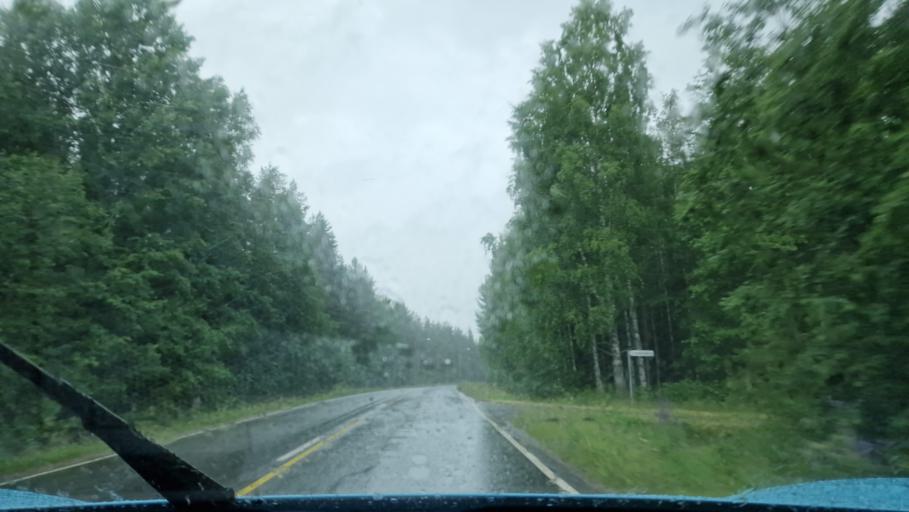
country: FI
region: Southern Ostrobothnia
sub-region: Jaerviseutu
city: Soini
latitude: 62.8342
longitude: 24.3332
